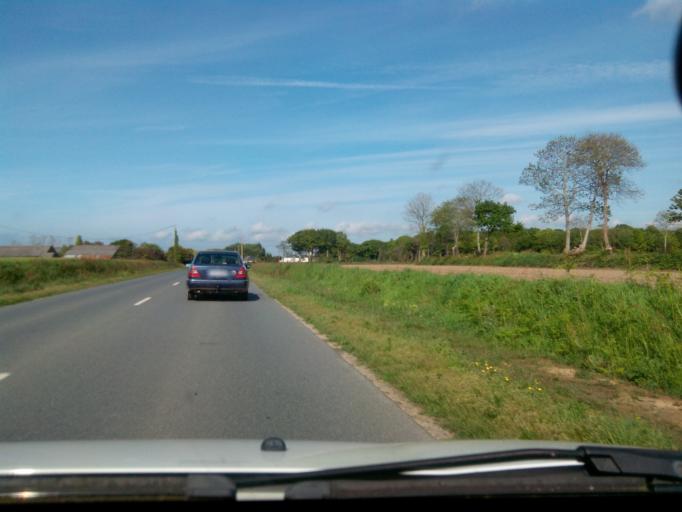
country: FR
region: Brittany
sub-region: Departement des Cotes-d'Armor
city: Louannec
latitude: 48.7804
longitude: -3.4043
